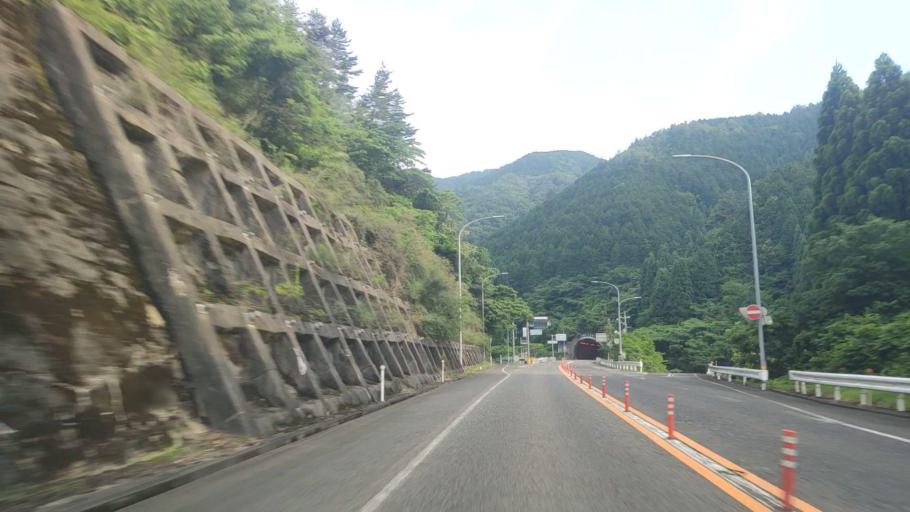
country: JP
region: Tottori
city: Kurayoshi
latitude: 35.3196
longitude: 133.7563
